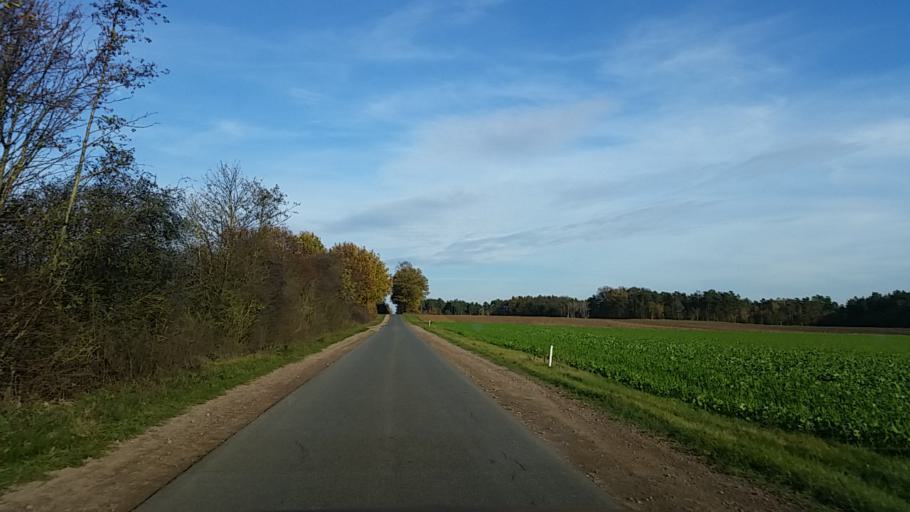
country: DE
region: Lower Saxony
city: Hankensbuttel
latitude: 52.6897
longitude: 10.5835
